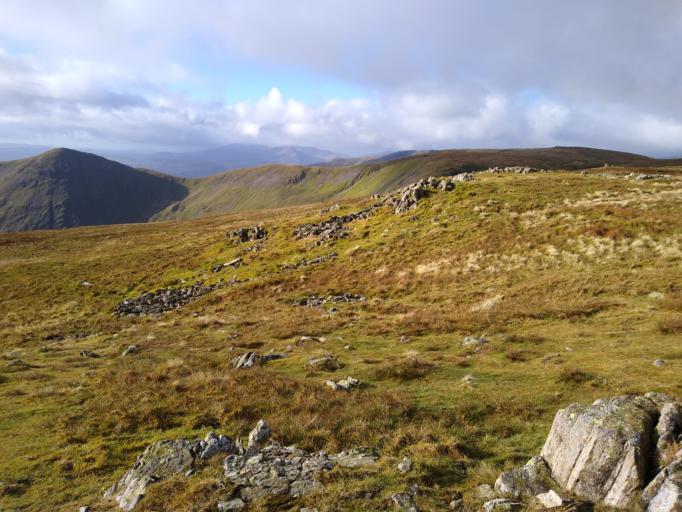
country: GB
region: England
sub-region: Cumbria
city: Windermere
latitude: 54.4830
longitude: -2.8540
